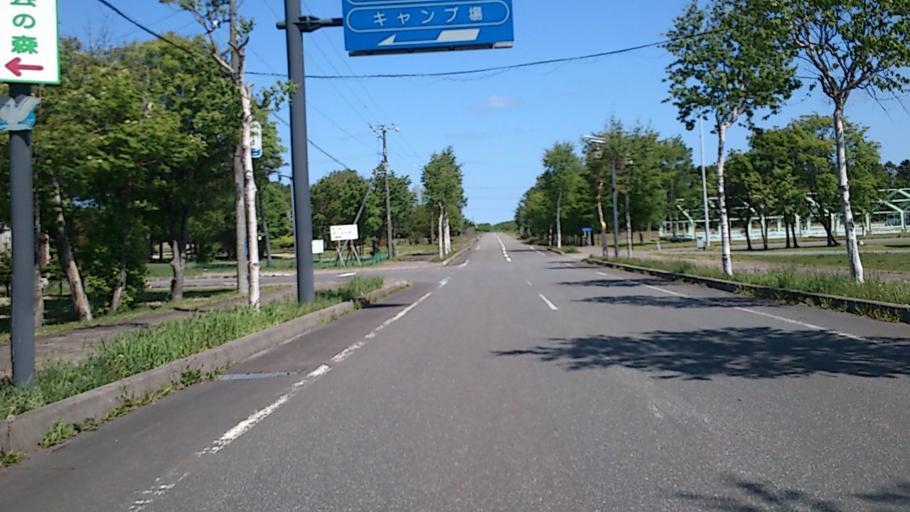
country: JP
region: Hokkaido
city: Makubetsu
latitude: 45.1242
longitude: 142.3503
